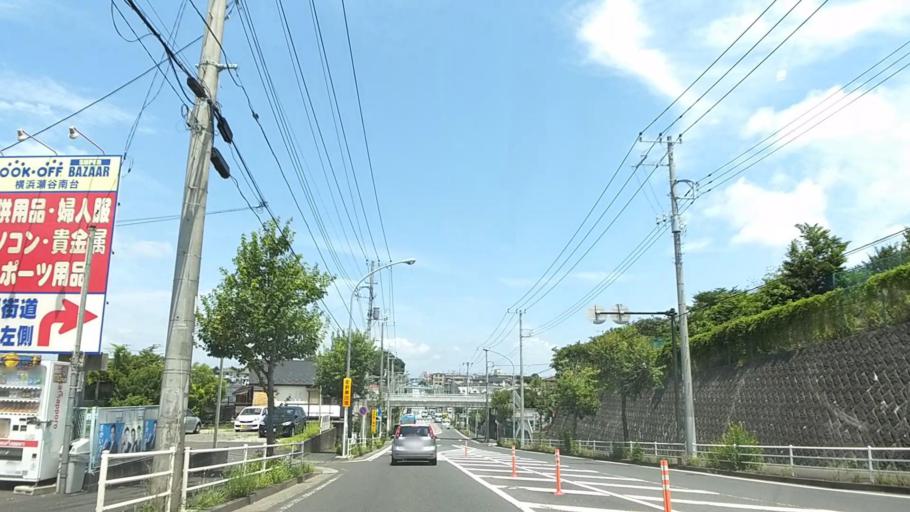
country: JP
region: Kanagawa
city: Minami-rinkan
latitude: 35.4512
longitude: 139.4832
